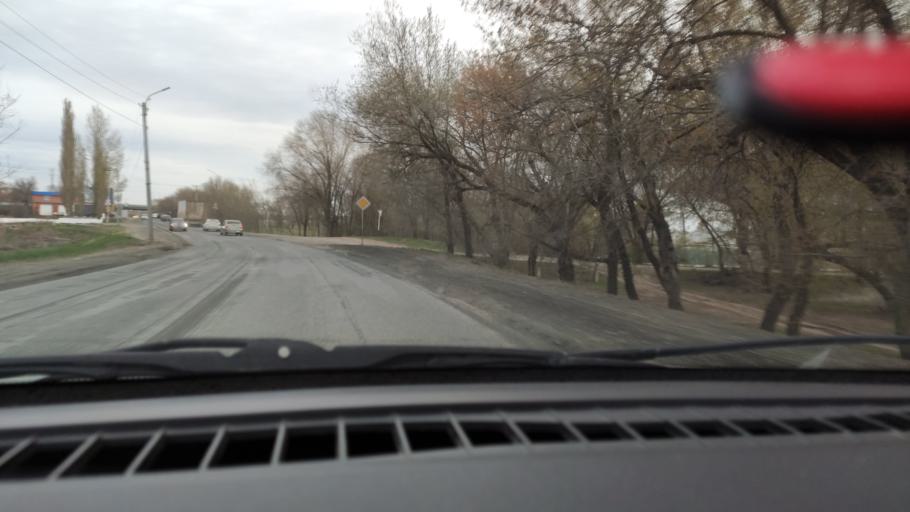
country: RU
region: Orenburg
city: Orenburg
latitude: 51.8594
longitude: 55.1341
